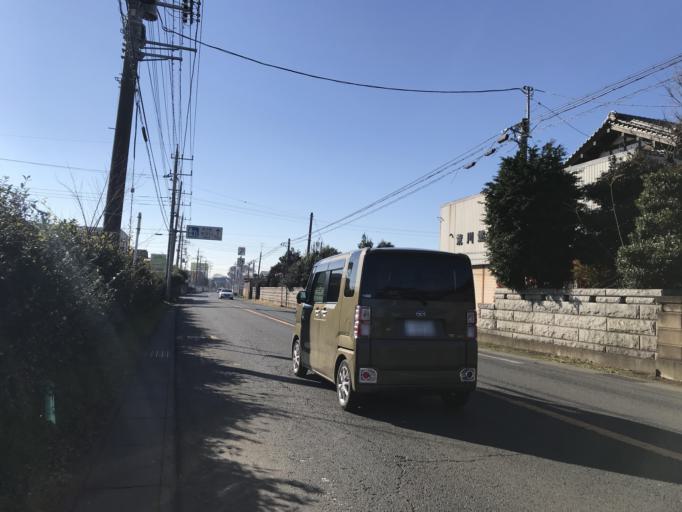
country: JP
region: Ibaraki
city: Sakai
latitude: 36.1913
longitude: 139.8115
